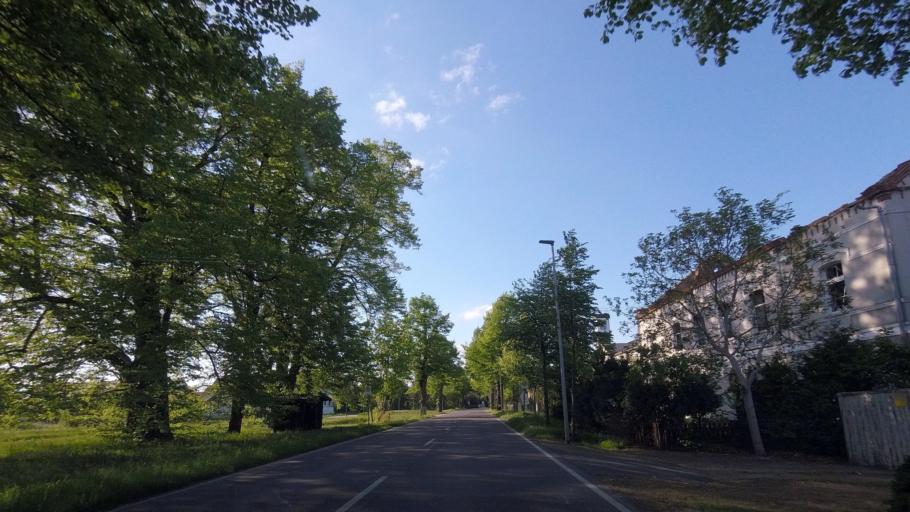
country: DE
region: Brandenburg
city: Lubbenau
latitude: 51.8851
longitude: 13.9030
